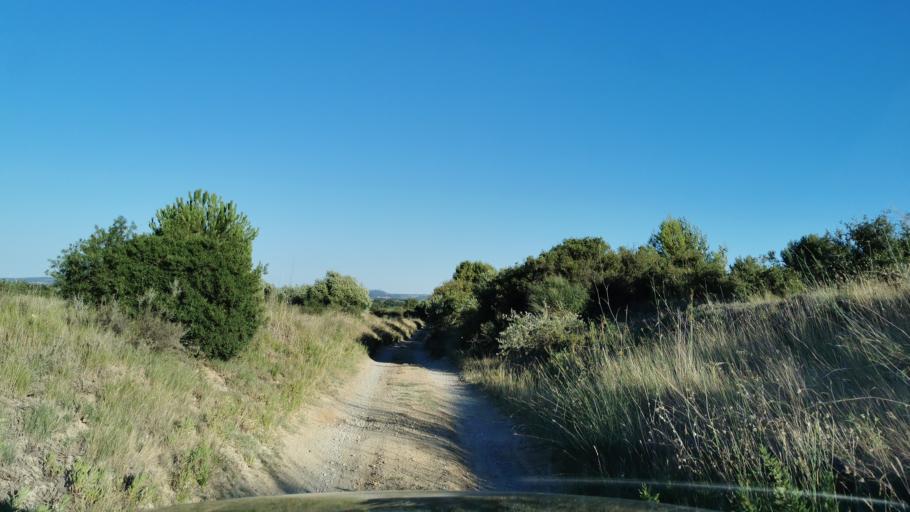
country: FR
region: Languedoc-Roussillon
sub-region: Departement de l'Aude
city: Ouveillan
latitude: 43.2706
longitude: 2.9784
